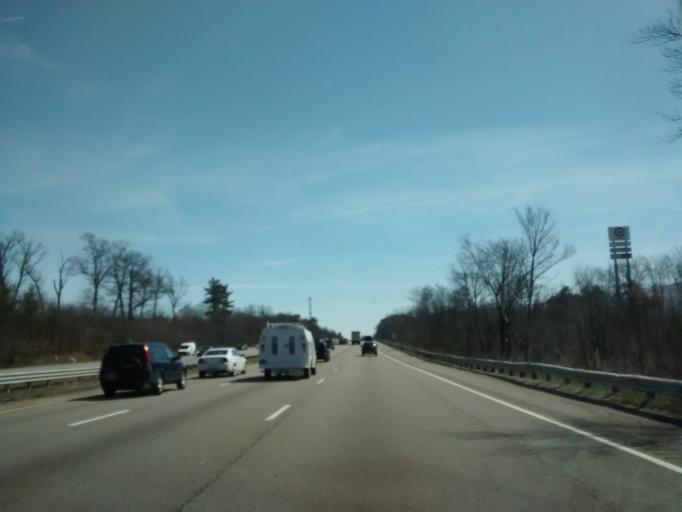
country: US
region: Massachusetts
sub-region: Norfolk County
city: Randolph
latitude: 42.1516
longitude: -71.0680
